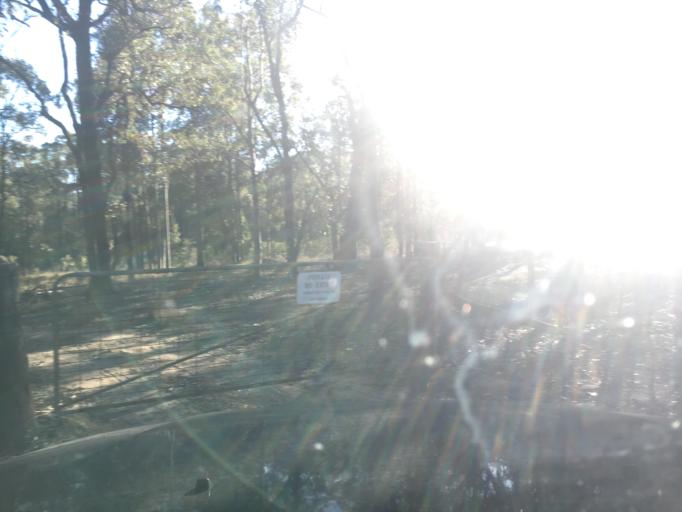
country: AU
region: New South Wales
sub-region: Singleton
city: Singleton
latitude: -32.5530
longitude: 151.2333
